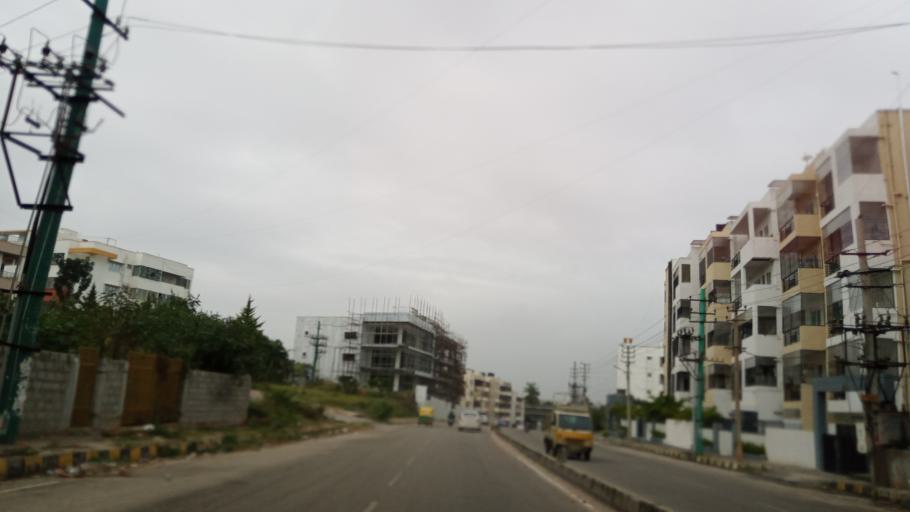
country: IN
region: Karnataka
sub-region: Bangalore Urban
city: Bangalore
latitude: 12.9074
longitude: 77.4905
